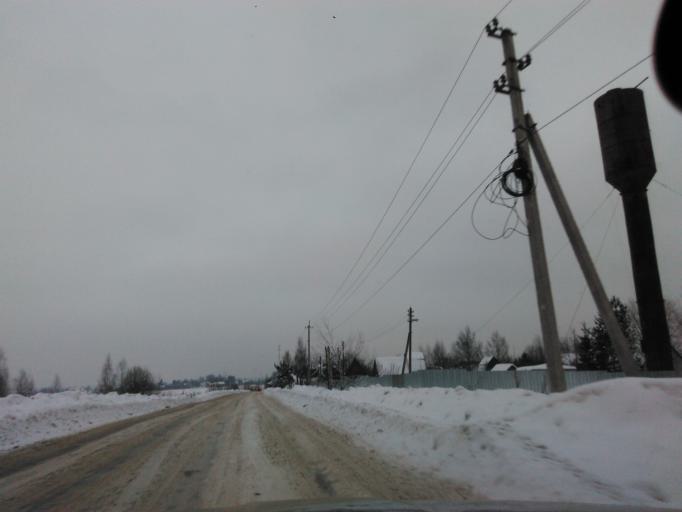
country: RU
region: Moskovskaya
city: Yakhroma
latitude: 56.2622
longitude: 37.4351
